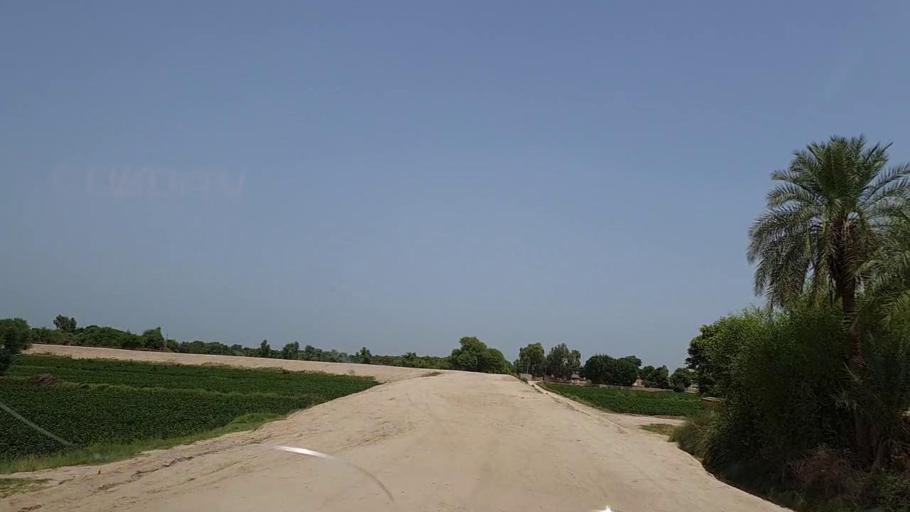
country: PK
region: Sindh
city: Tharu Shah
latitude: 27.0224
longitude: 68.1156
